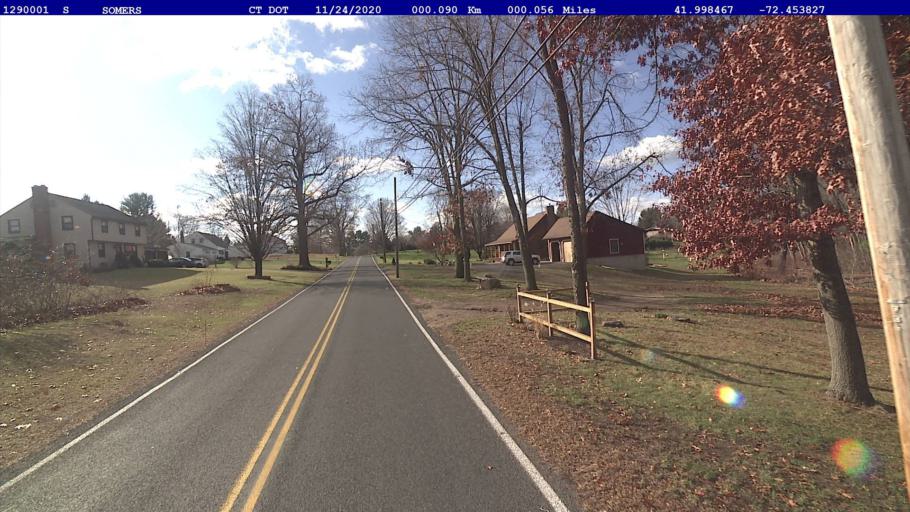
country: US
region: Connecticut
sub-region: Tolland County
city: Somers
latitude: 41.9985
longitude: -72.4538
